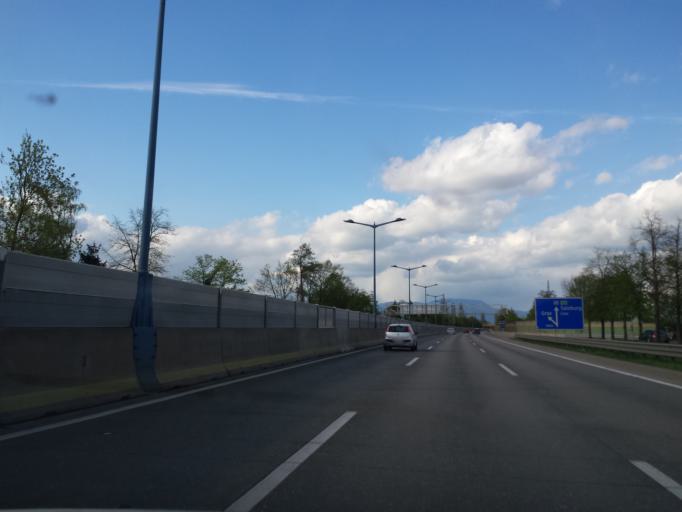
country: AT
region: Styria
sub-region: Politischer Bezirk Graz-Umgebung
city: Seiersberg
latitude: 47.0171
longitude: 15.4086
